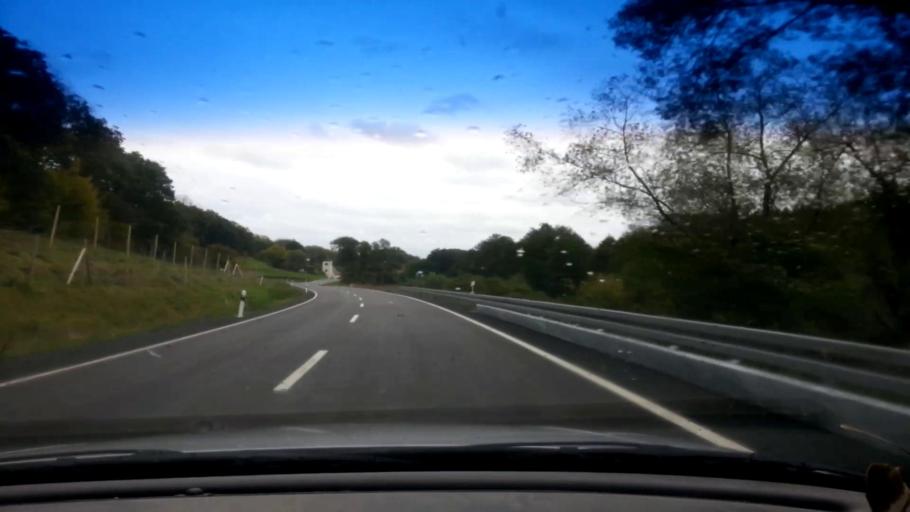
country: DE
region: Bavaria
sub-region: Regierungsbezirk Unterfranken
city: Kirchlauter
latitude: 50.0151
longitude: 10.7353
